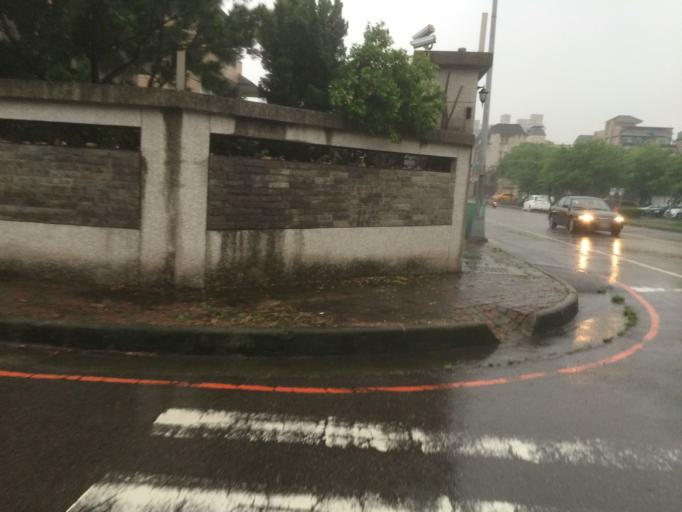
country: TW
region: Taiwan
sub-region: Taichung City
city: Taichung
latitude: 24.1792
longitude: 120.7156
